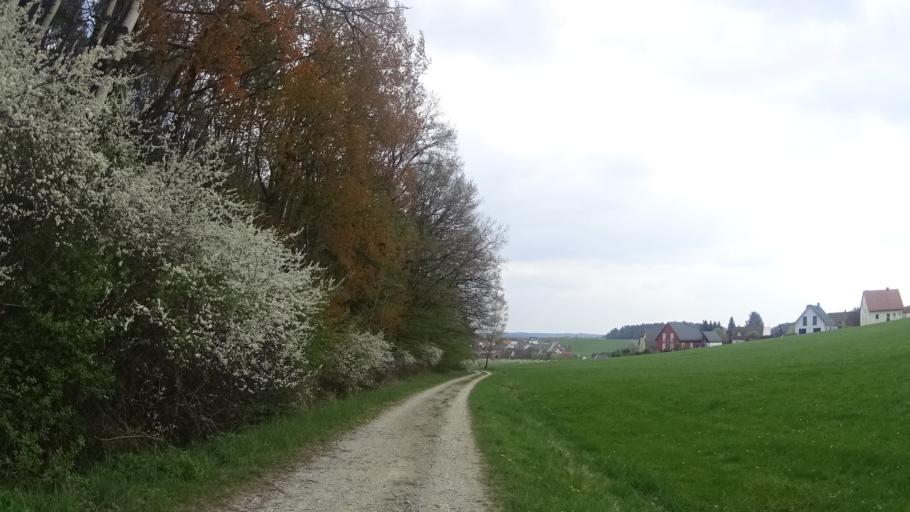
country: DE
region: Bavaria
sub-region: Upper Franconia
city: Igensdorf
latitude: 49.6218
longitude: 11.2169
